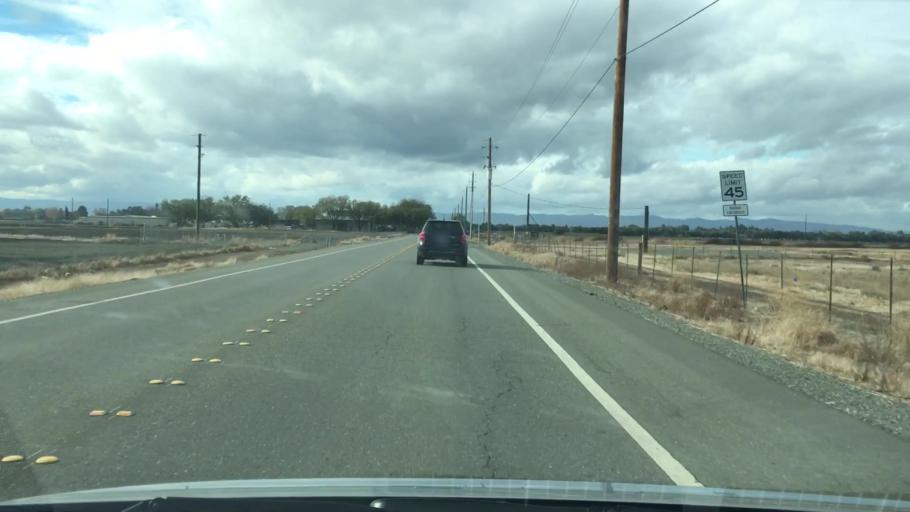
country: US
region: California
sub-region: Yolo County
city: Davis
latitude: 38.5394
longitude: -121.7749
